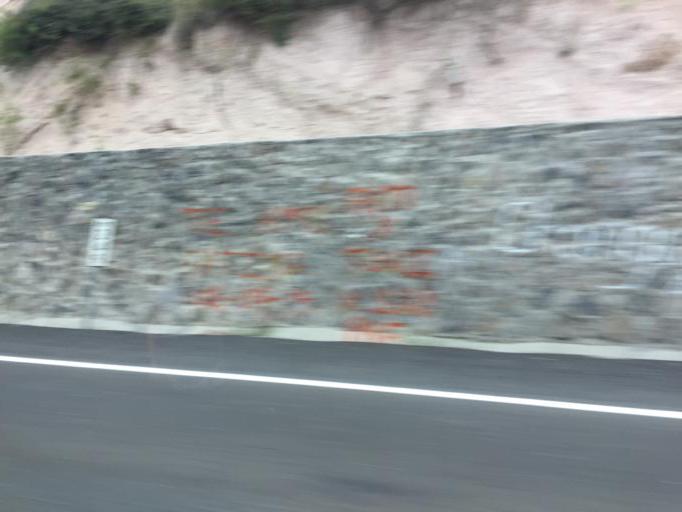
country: MX
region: Michoacan
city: Copandaro de Galeana
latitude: 19.8860
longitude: -101.2280
